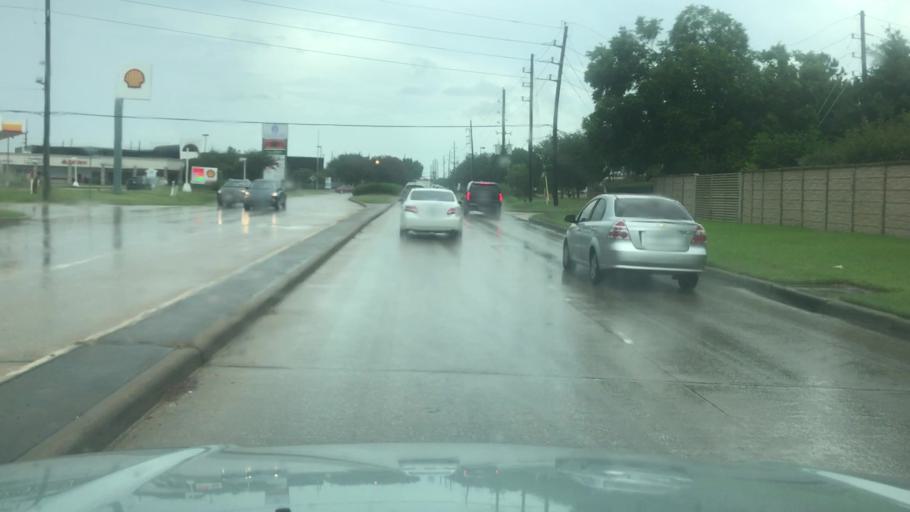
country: US
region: Texas
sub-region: Harris County
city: Katy
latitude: 29.7695
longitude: -95.8172
